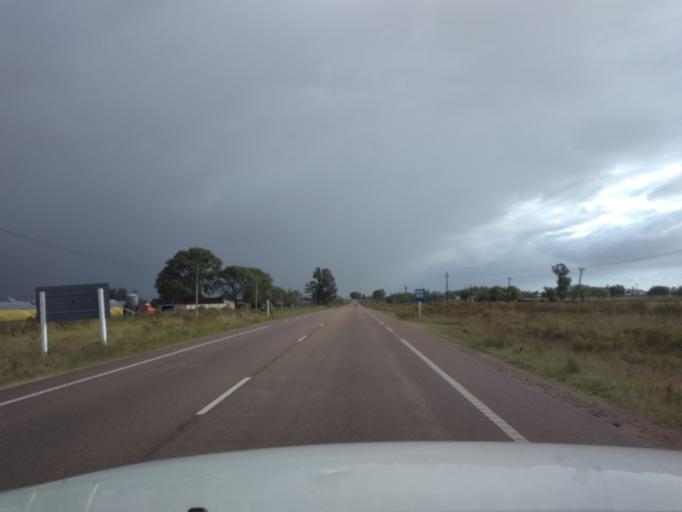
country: UY
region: Canelones
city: Tala
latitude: -34.3727
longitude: -55.7864
